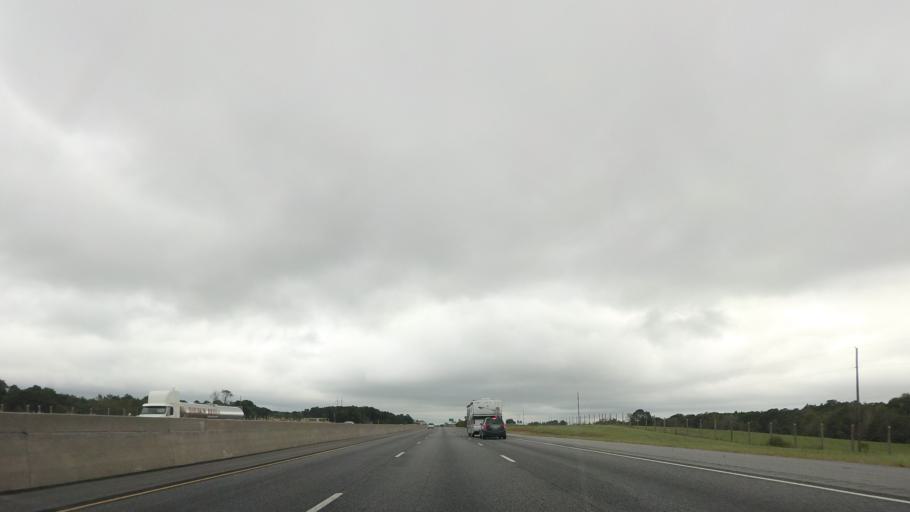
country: US
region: Georgia
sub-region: Tift County
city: Tifton
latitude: 31.5907
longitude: -83.5580
